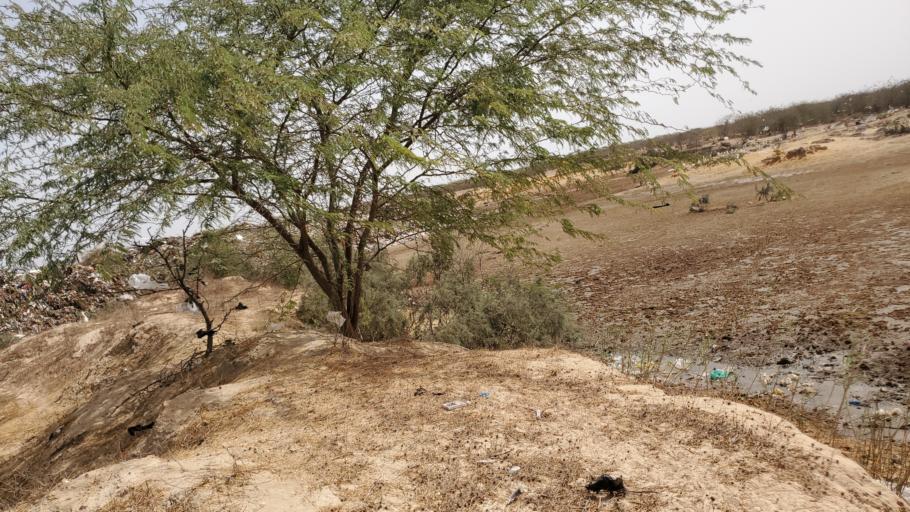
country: SN
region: Saint-Louis
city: Saint-Louis
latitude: 15.9478
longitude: -16.4304
